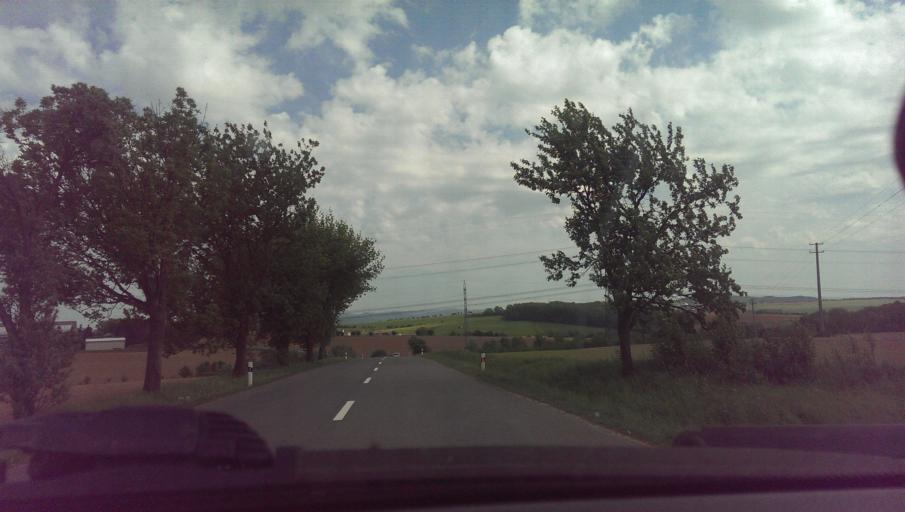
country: CZ
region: Zlin
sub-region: Okres Zlin
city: Otrokovice
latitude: 49.2447
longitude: 17.5400
